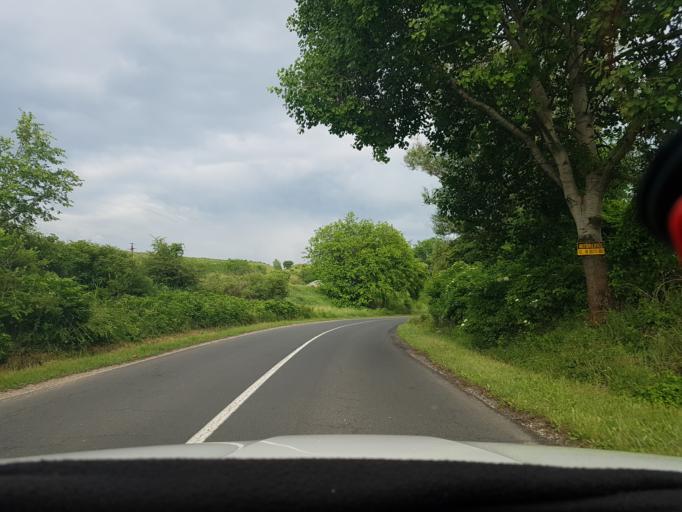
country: HU
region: Komarom-Esztergom
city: Tokod
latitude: 47.7071
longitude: 18.6378
